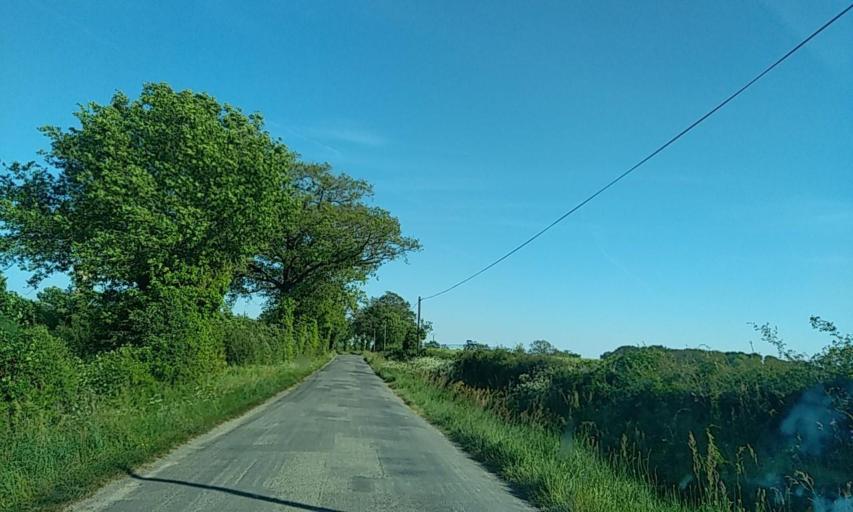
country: FR
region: Poitou-Charentes
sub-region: Departement des Deux-Sevres
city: Boisme
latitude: 46.7958
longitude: -0.4334
